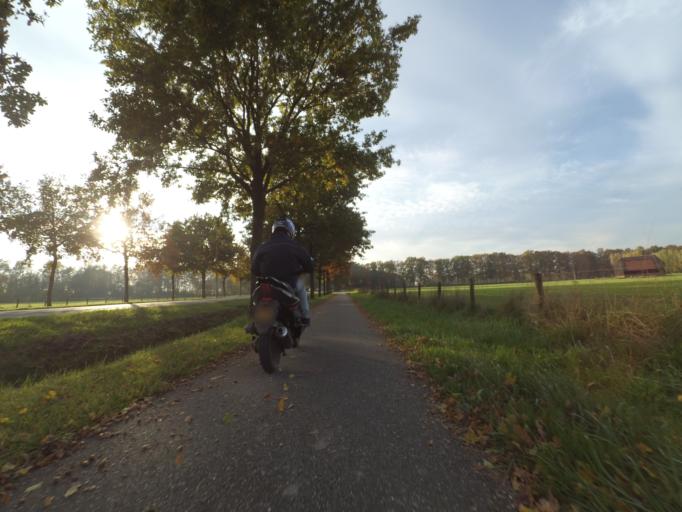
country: NL
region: Utrecht
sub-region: Gemeente Utrechtse Heuvelrug
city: Overberg
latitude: 52.0763
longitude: 5.5182
